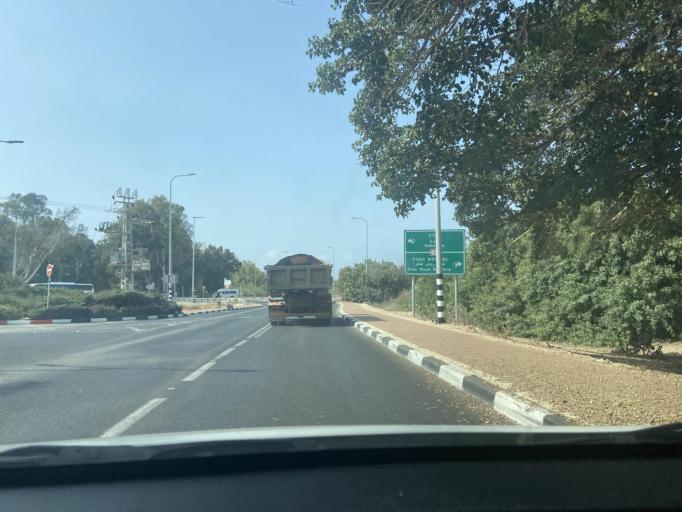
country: IL
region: Northern District
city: Nahariya
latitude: 33.0449
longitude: 35.1071
